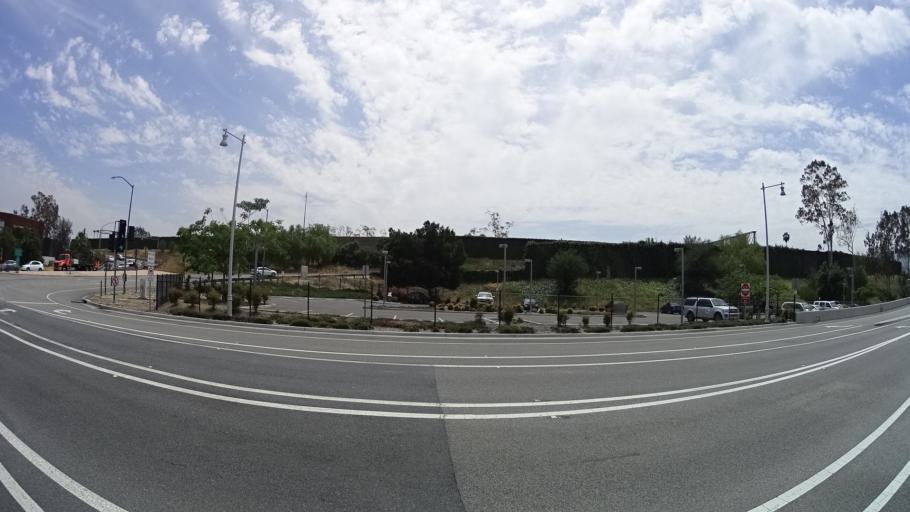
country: US
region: California
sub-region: Los Angeles County
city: North Glendale
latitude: 34.1551
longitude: -118.2743
